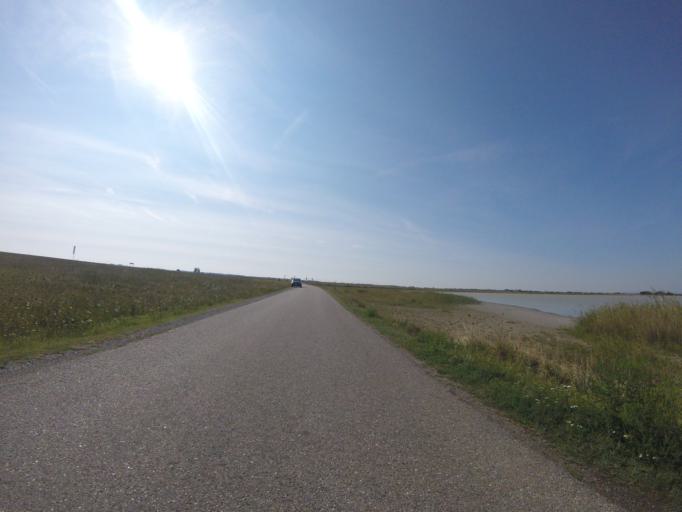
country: AT
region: Burgenland
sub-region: Politischer Bezirk Neusiedl am See
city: Apetlon
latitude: 47.7729
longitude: 16.8444
